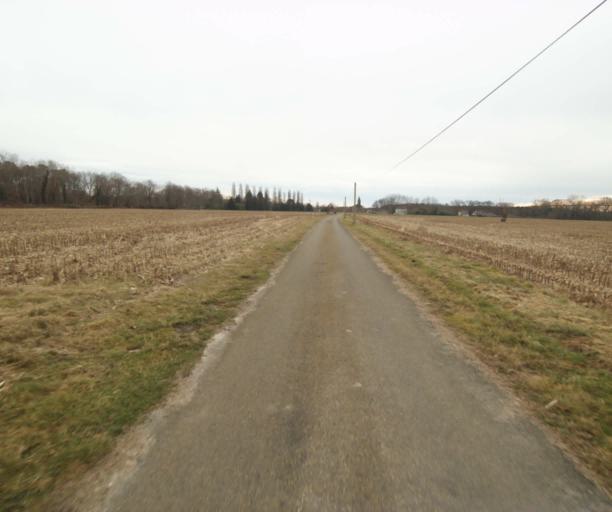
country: FR
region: Aquitaine
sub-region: Departement des Landes
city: Gabarret
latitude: 44.0100
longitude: -0.0310
